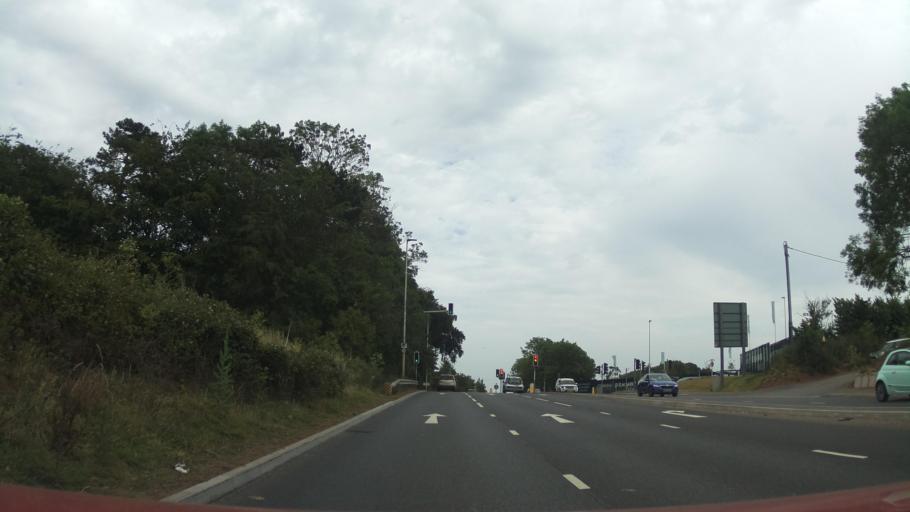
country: GB
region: England
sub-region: Devon
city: Exminster
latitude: 50.6925
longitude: -3.5143
